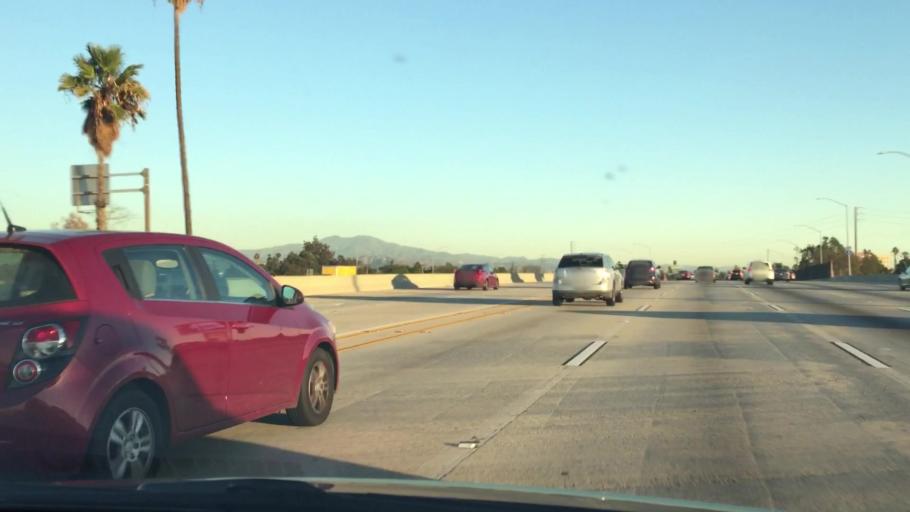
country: US
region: California
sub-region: Orange County
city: Santa Ana
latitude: 33.7518
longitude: -117.8525
